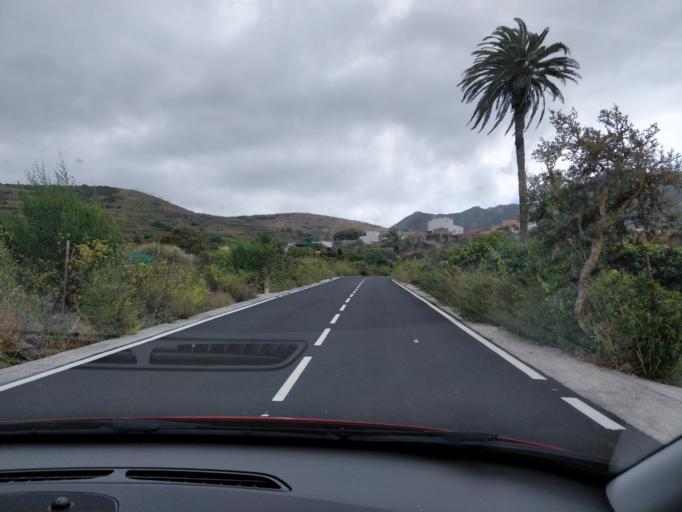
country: ES
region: Canary Islands
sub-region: Provincia de Santa Cruz de Tenerife
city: Tanque
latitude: 28.3464
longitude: -16.8444
